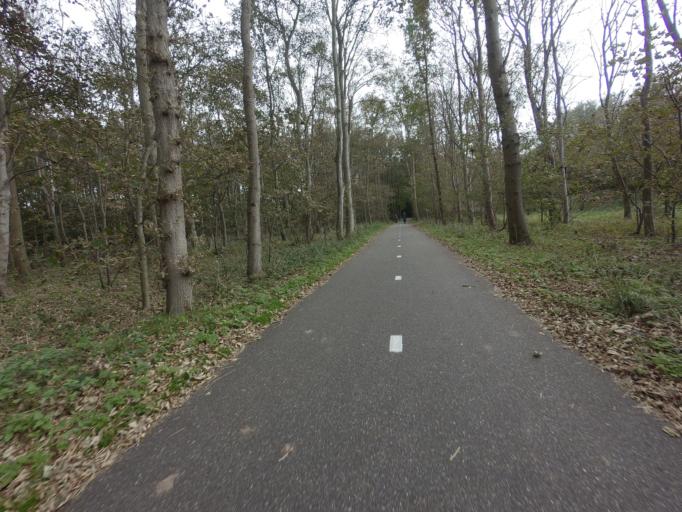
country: NL
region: Zeeland
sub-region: Gemeente Vlissingen
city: Vlissingen
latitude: 51.4889
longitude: 3.5076
